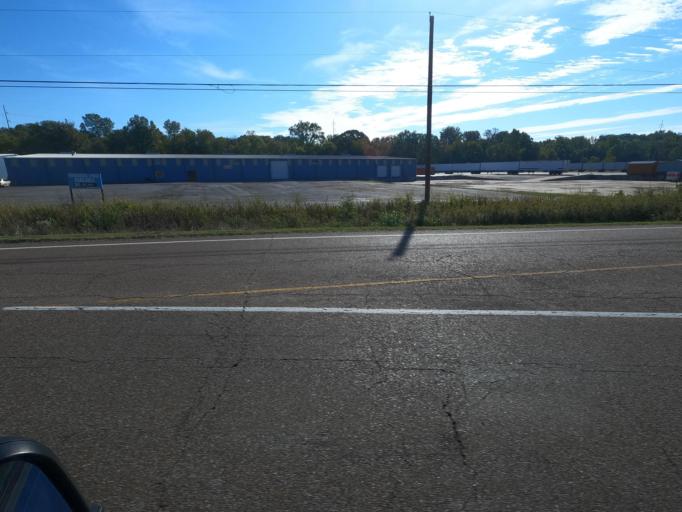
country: US
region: Tennessee
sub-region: Tipton County
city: Brighton
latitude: 35.4939
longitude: -89.7239
